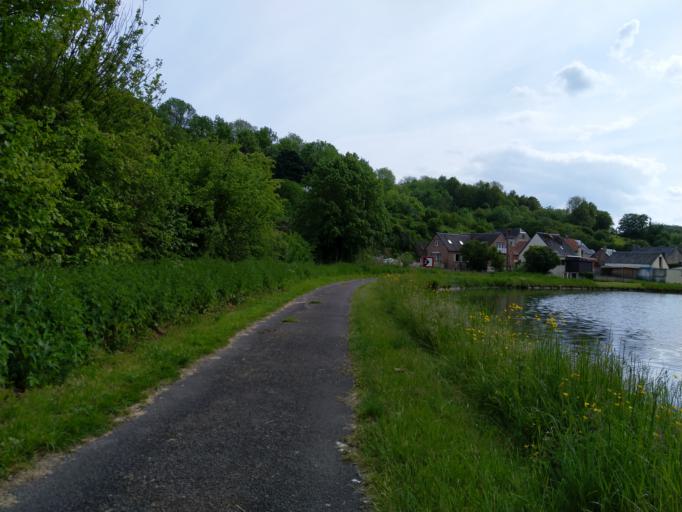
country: FR
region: Picardie
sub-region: Departement de l'Aisne
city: Etreux
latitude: 49.9545
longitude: 3.6080
